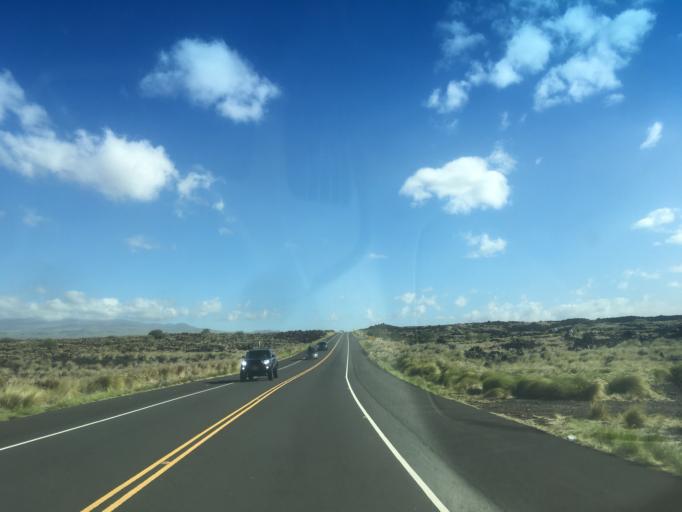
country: US
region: Hawaii
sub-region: Hawaii County
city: Waikoloa Village
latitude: 19.9147
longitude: -155.8238
